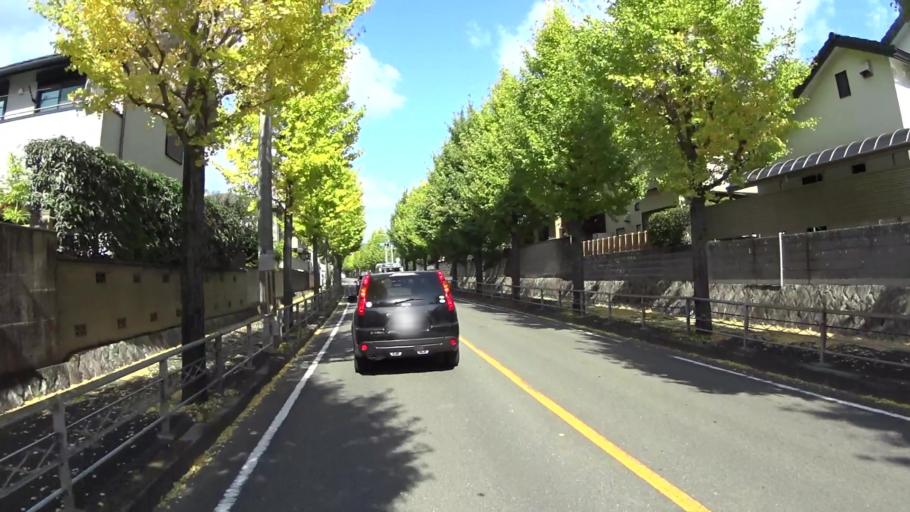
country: JP
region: Kyoto
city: Muko
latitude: 34.9574
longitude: 135.6866
